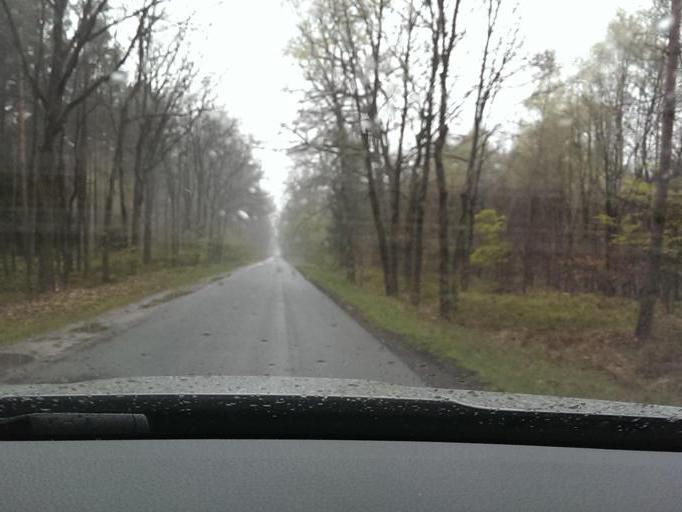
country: DE
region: Lower Saxony
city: Elze
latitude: 52.6078
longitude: 9.7714
